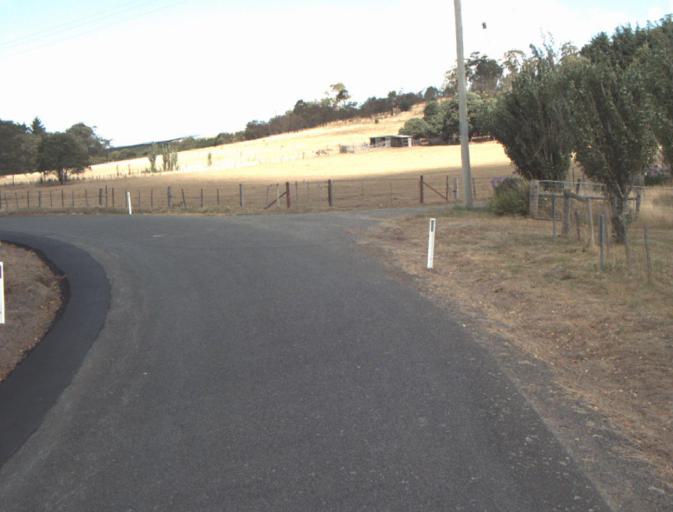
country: AU
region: Tasmania
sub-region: Launceston
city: Mayfield
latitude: -41.3026
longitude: 147.0349
